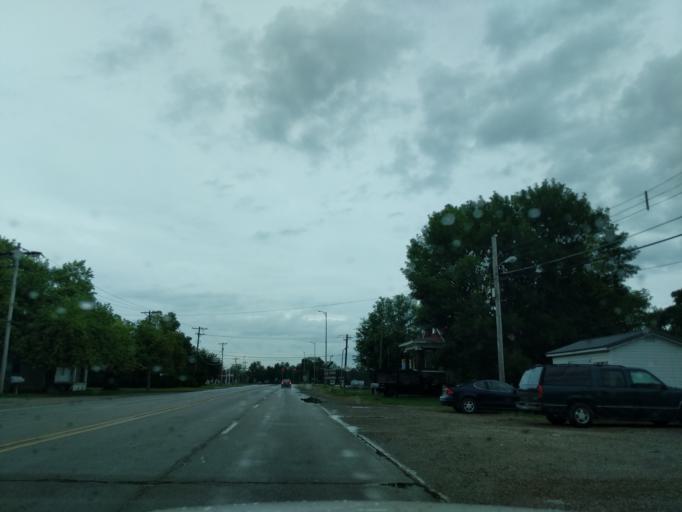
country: US
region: Illinois
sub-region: Saint Clair County
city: Fairmont City
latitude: 38.6594
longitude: -90.0889
